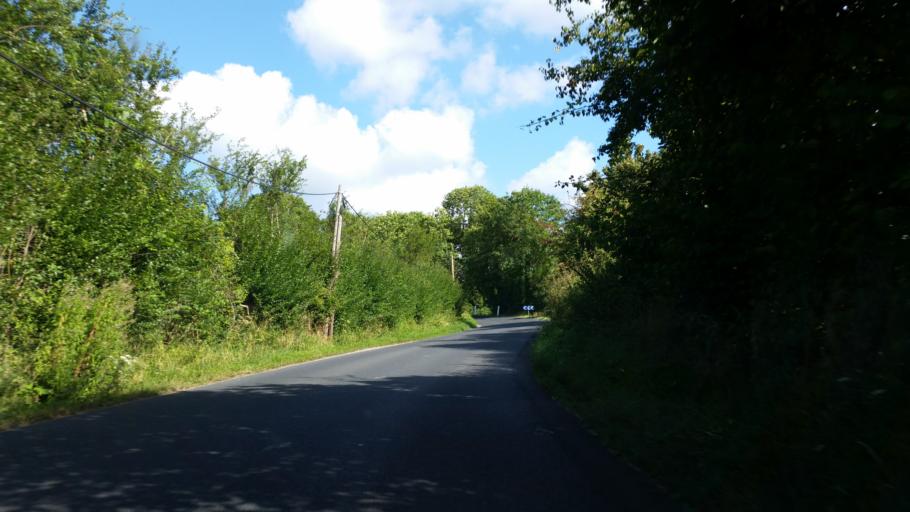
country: FR
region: Lower Normandy
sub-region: Departement du Calvados
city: Touques
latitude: 49.3385
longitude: 0.1146
